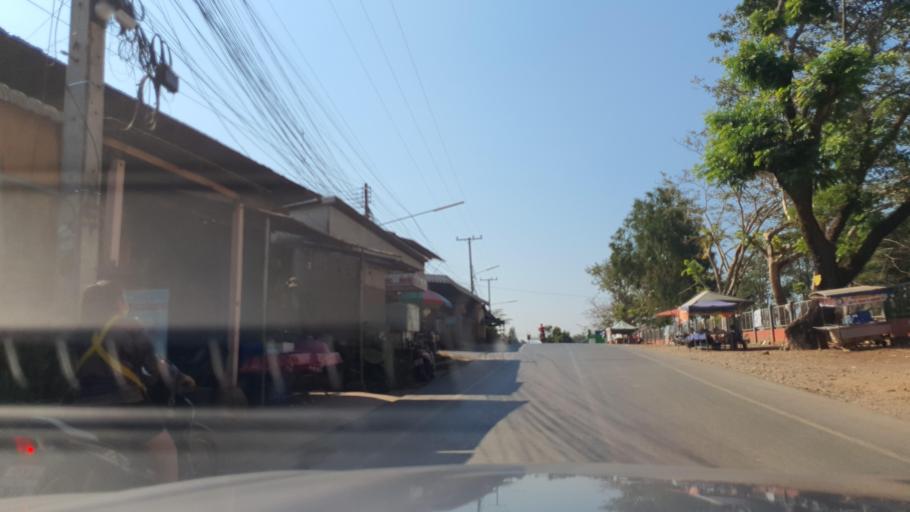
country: TH
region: Nan
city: Pua
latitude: 19.1399
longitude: 100.9338
